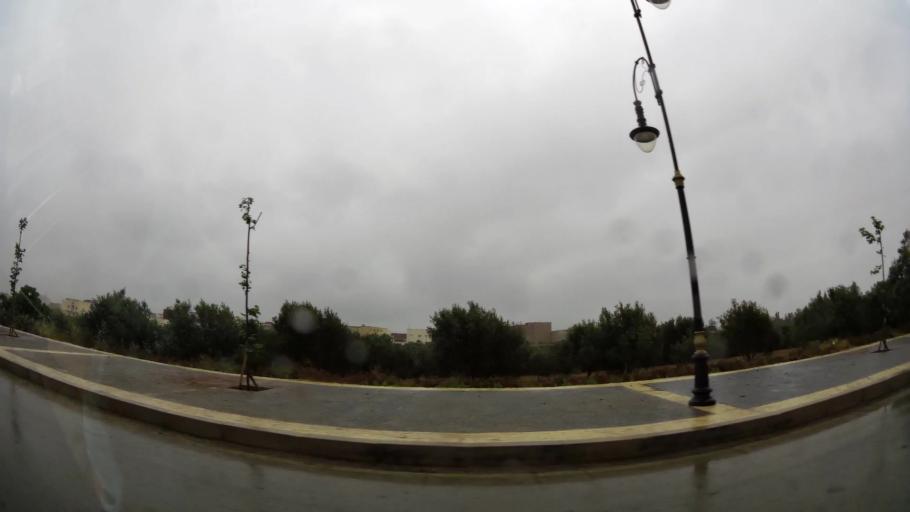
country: MA
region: Taza-Al Hoceima-Taounate
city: Imzourene
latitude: 35.1388
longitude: -3.8475
